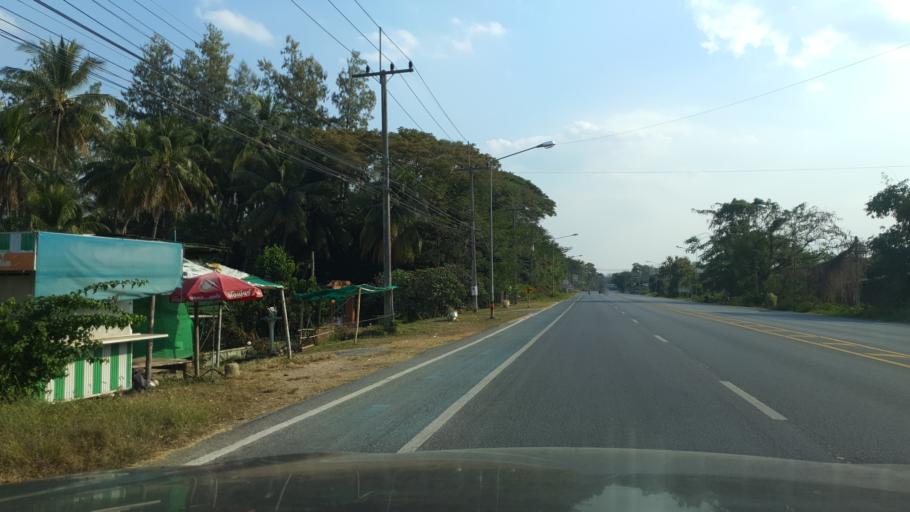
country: TH
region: Tak
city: Tak
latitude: 16.8636
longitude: 99.1205
